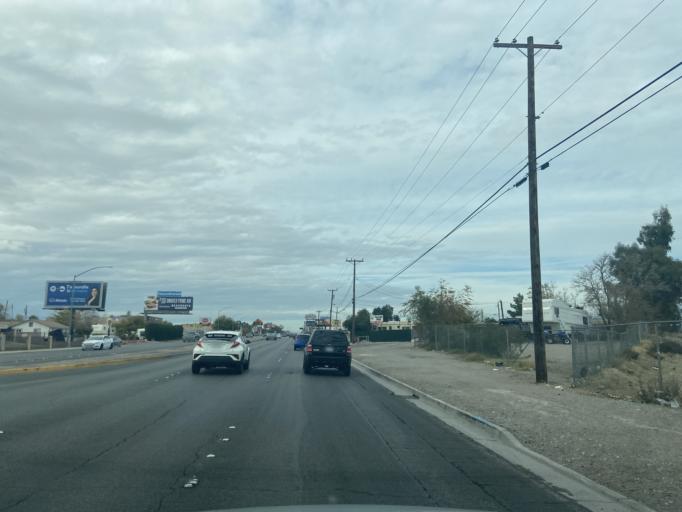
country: US
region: Nevada
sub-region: Clark County
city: Las Vegas
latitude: 36.1907
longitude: -115.1878
